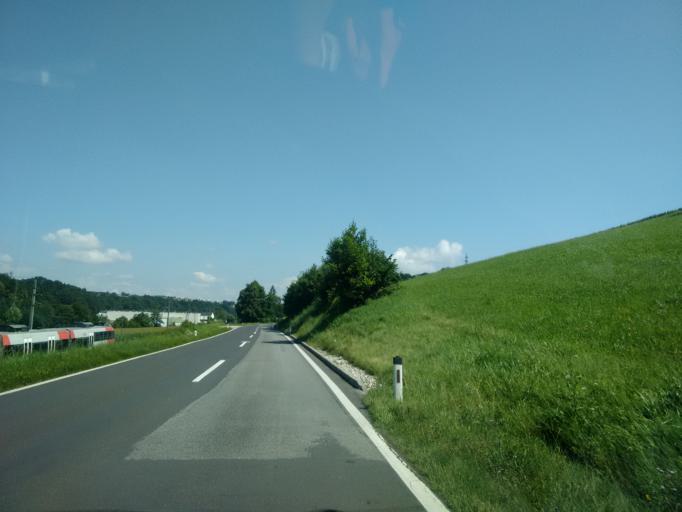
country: AT
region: Upper Austria
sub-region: Politischer Bezirk Kirchdorf an der Krems
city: Kremsmunster
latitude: 48.0311
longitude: 14.1216
